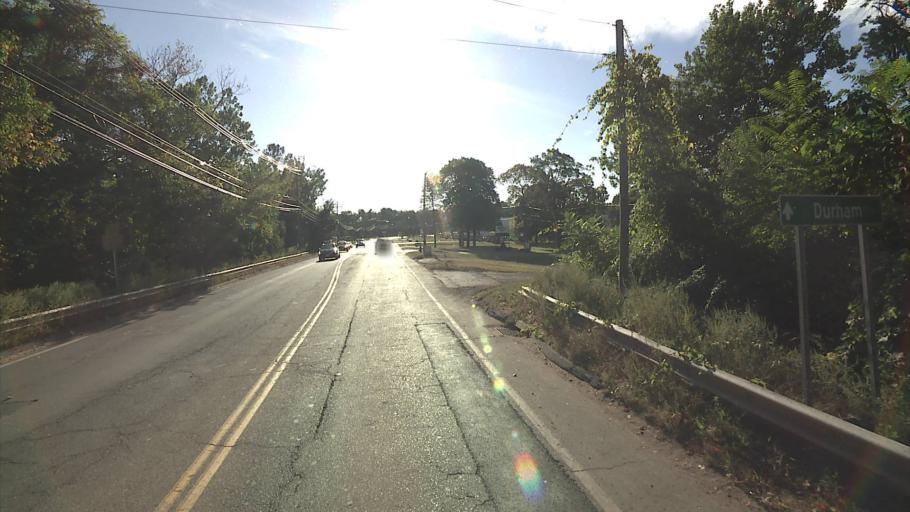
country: US
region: Connecticut
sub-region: New Haven County
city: Wallingford
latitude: 41.4909
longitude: -72.8166
